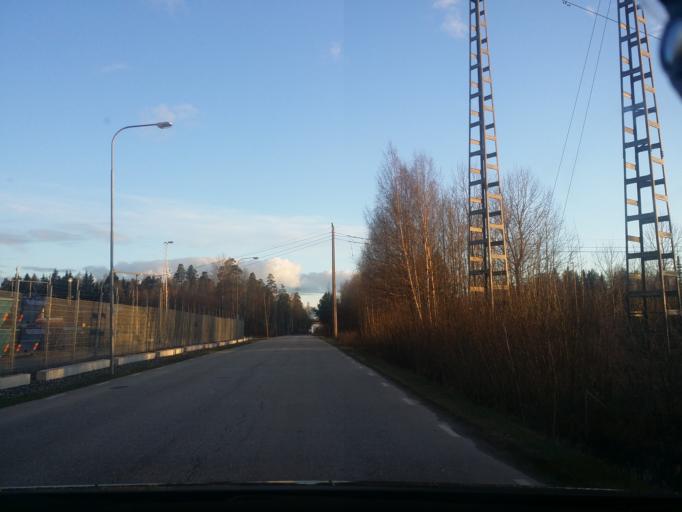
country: SE
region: Vaestmanland
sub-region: Vasteras
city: Hokasen
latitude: 59.6460
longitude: 16.5842
